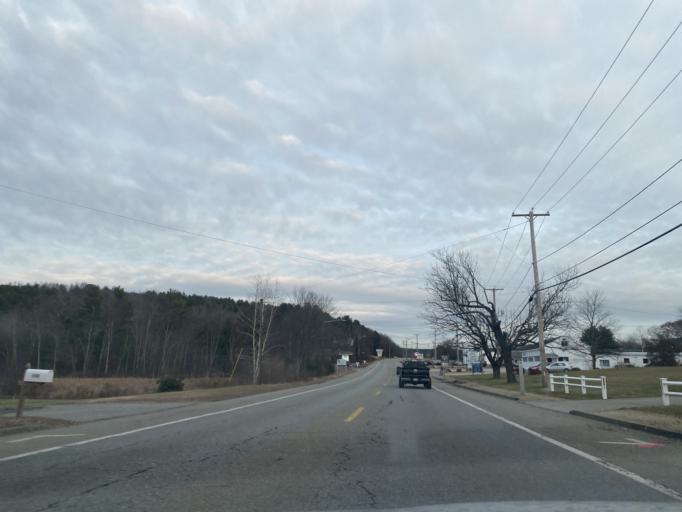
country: US
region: Massachusetts
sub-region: Worcester County
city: East Brookfield
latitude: 42.2316
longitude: -72.0275
